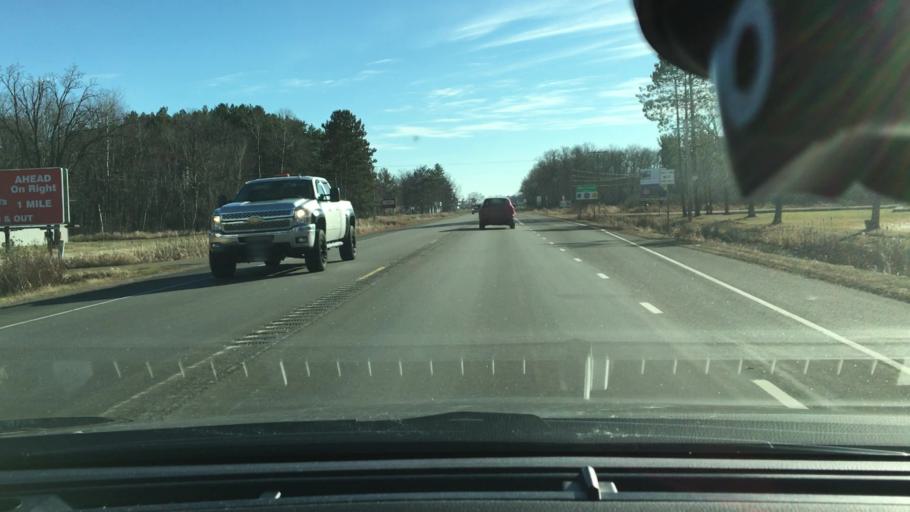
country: US
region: Minnesota
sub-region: Mille Lacs County
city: Vineland
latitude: 46.3023
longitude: -93.8288
